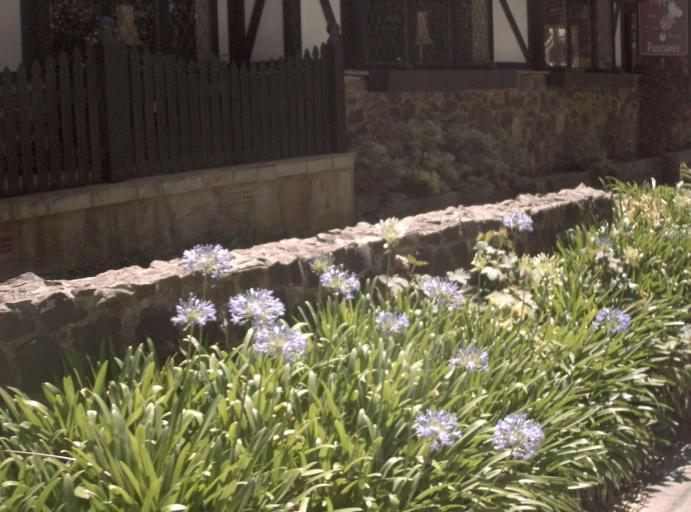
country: AU
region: Victoria
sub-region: Yarra Ranges
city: Kallista
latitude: -37.8678
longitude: 145.3530
